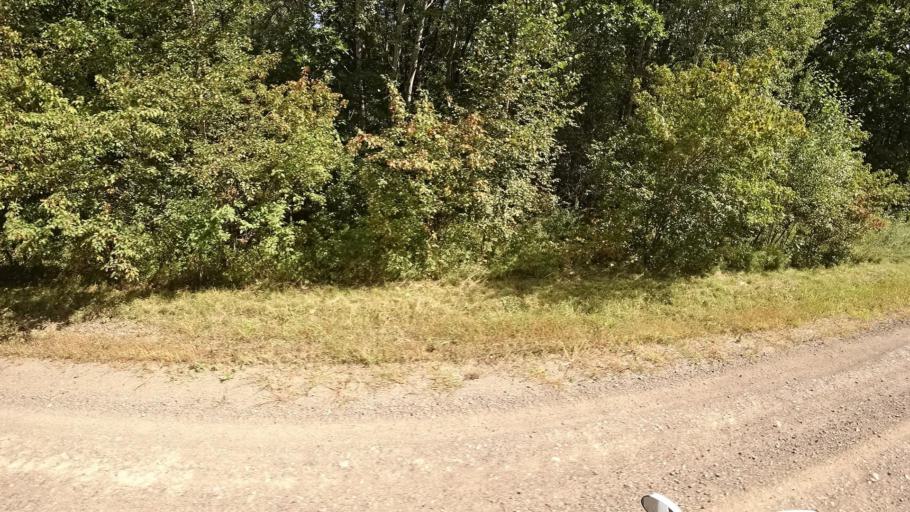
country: RU
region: Primorskiy
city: Yakovlevka
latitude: 44.7019
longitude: 133.6428
